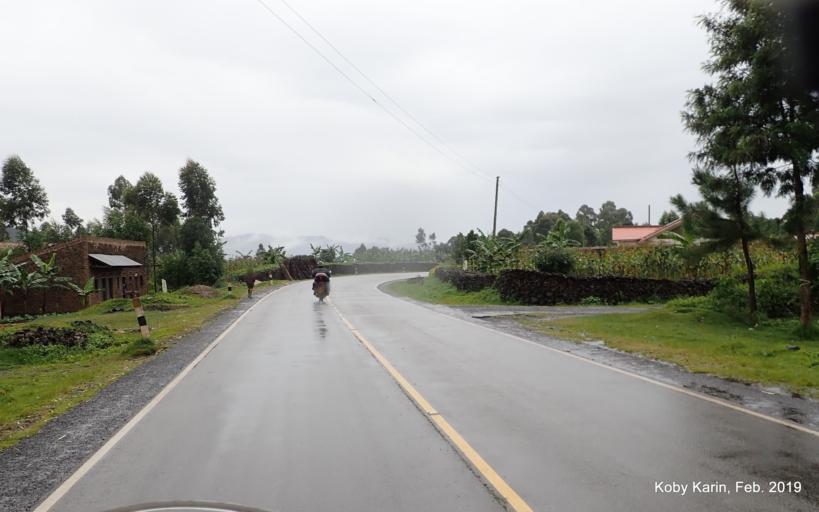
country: UG
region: Western Region
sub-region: Kisoro District
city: Kisoro
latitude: -1.3157
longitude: 29.7248
